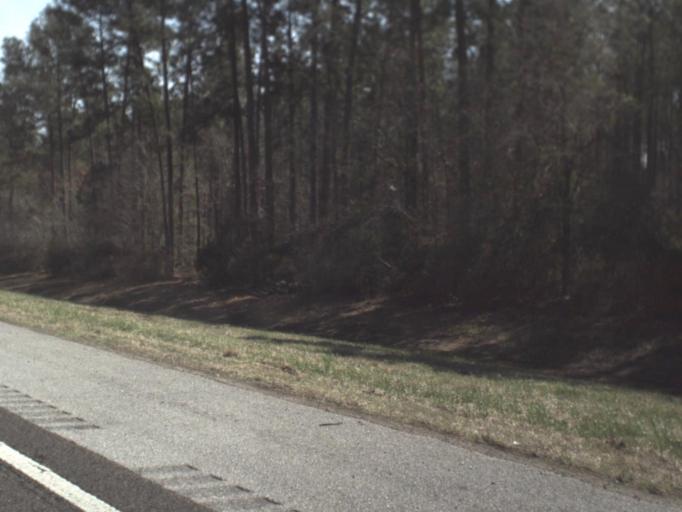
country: US
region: Florida
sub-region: Holmes County
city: Bonifay
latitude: 30.7610
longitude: -85.6530
